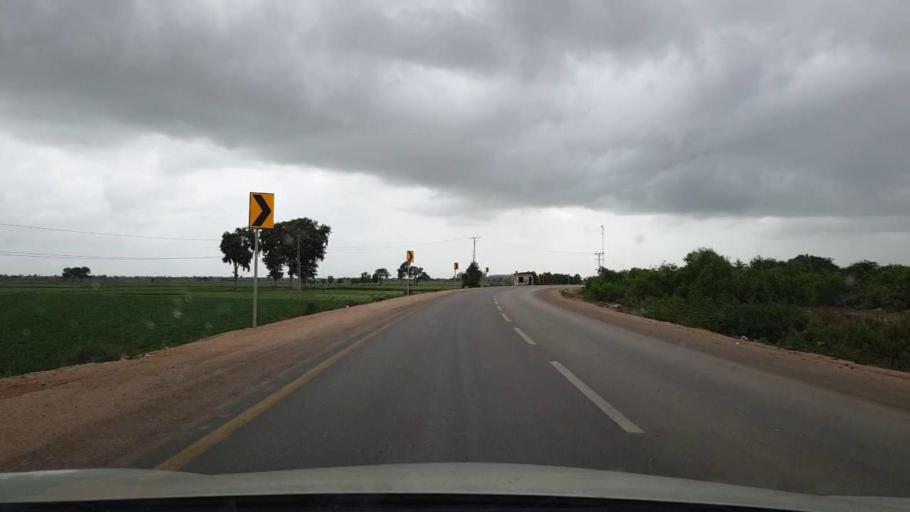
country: PK
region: Sindh
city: Kario
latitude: 24.6517
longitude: 68.4986
